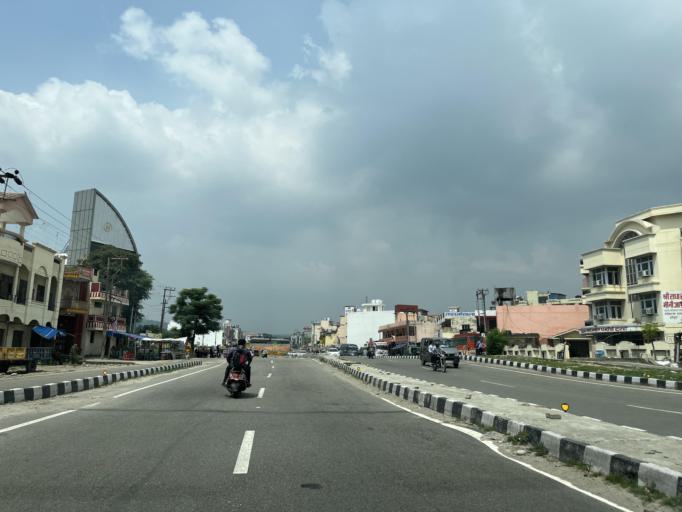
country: IN
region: Uttarakhand
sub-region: Haridwar
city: Haridwar
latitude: 29.9775
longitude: 78.1825
